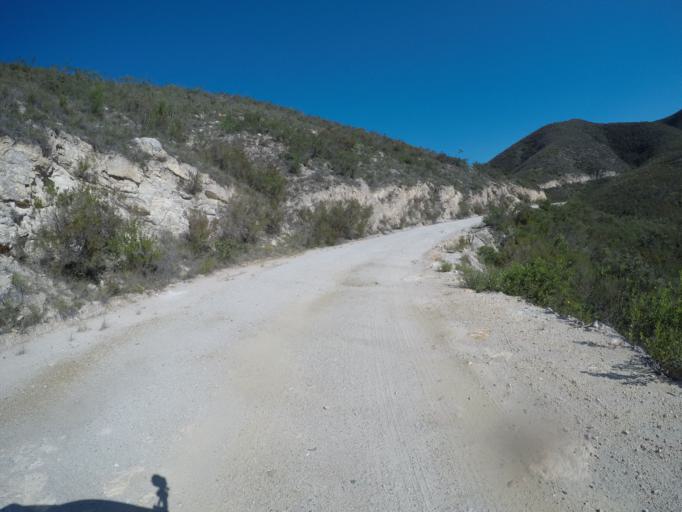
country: ZA
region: Eastern Cape
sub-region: Cacadu District Municipality
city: Kareedouw
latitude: -33.6535
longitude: 24.5009
